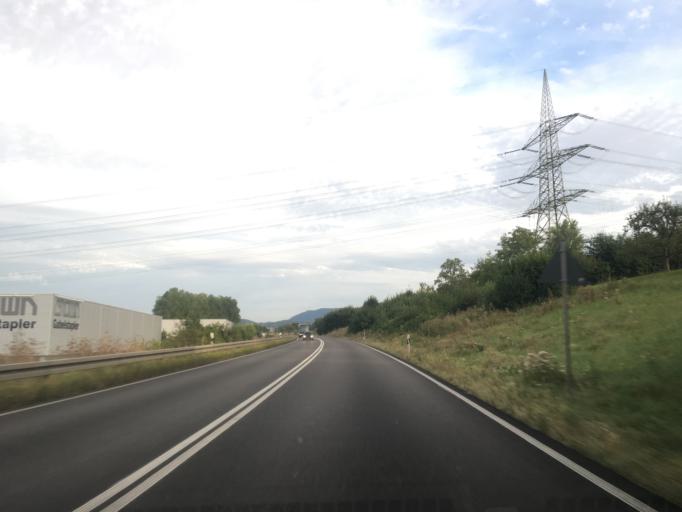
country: DE
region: Baden-Wuerttemberg
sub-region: Regierungsbezirk Stuttgart
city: Bempflingen
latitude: 48.5768
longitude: 9.2533
